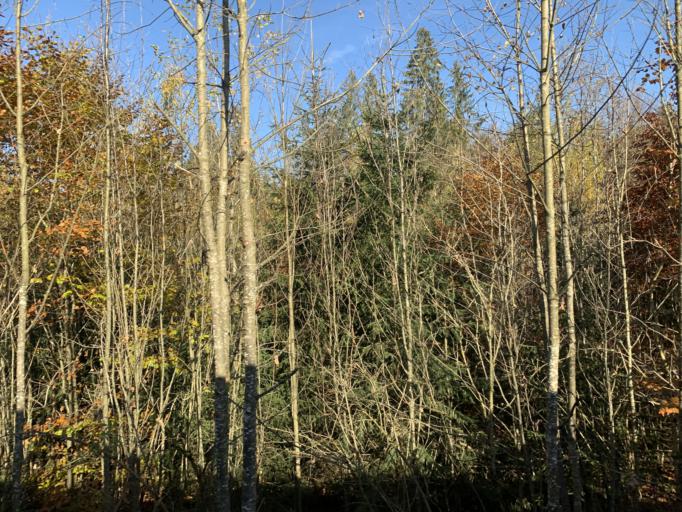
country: DE
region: Bavaria
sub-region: Upper Bavaria
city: Waakirchen
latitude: 47.7975
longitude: 11.6878
